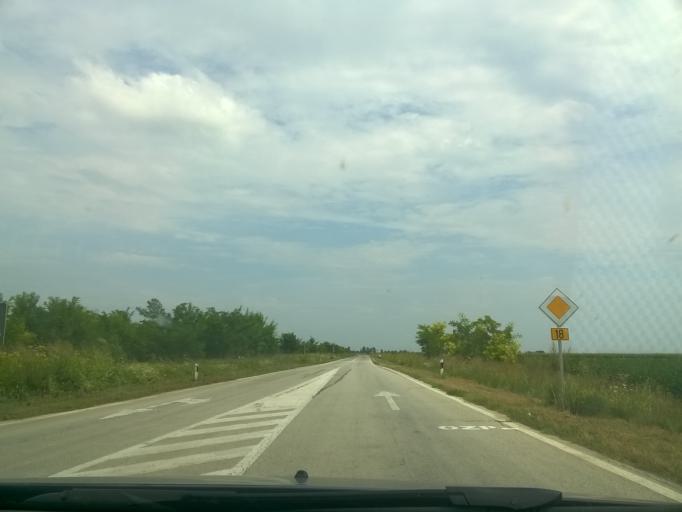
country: RS
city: Velika Greda
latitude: 45.2312
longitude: 21.0036
